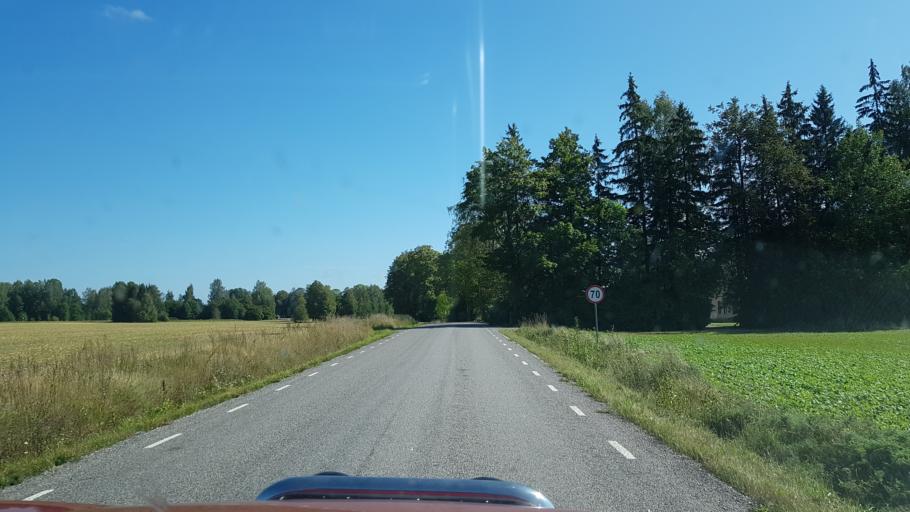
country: EE
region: Polvamaa
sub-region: Polva linn
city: Polva
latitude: 58.2094
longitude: 27.2475
